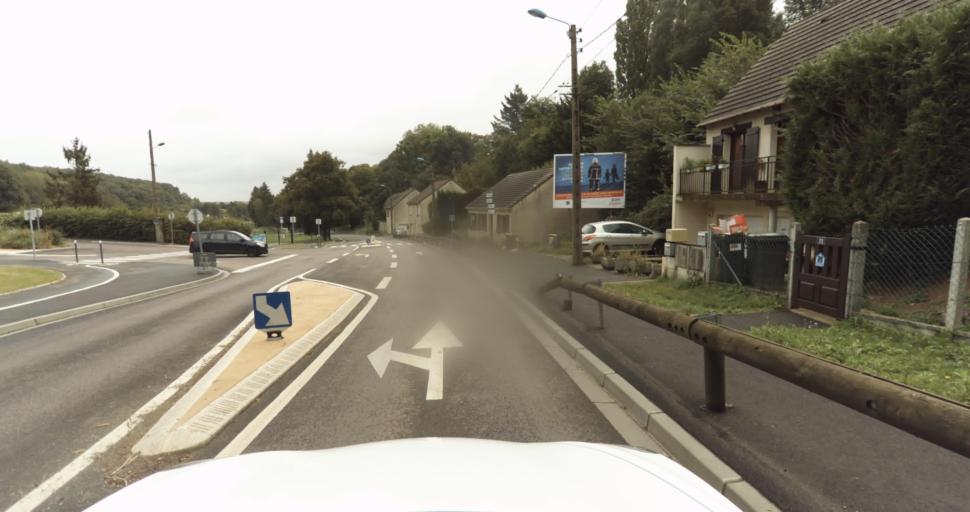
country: FR
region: Haute-Normandie
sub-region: Departement de l'Eure
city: Evreux
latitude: 49.0326
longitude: 1.1444
